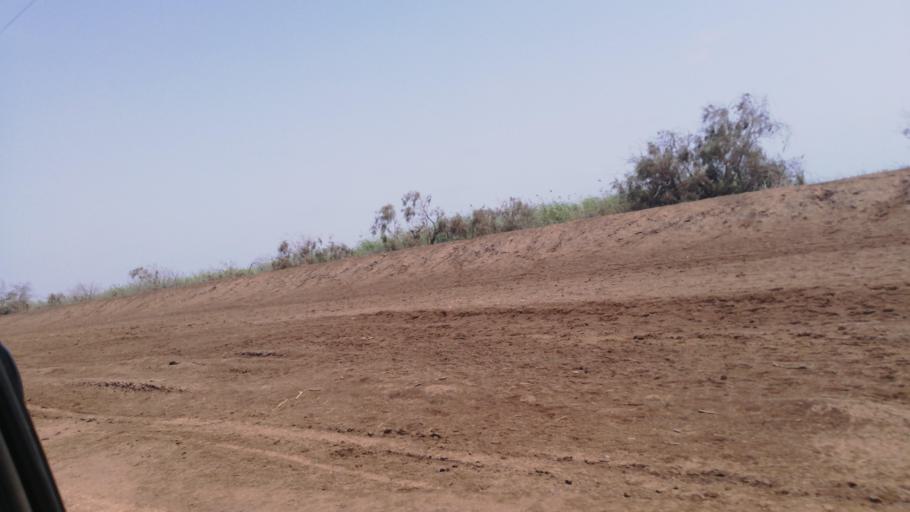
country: SN
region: Saint-Louis
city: Saint-Louis
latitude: 16.4026
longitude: -16.2923
